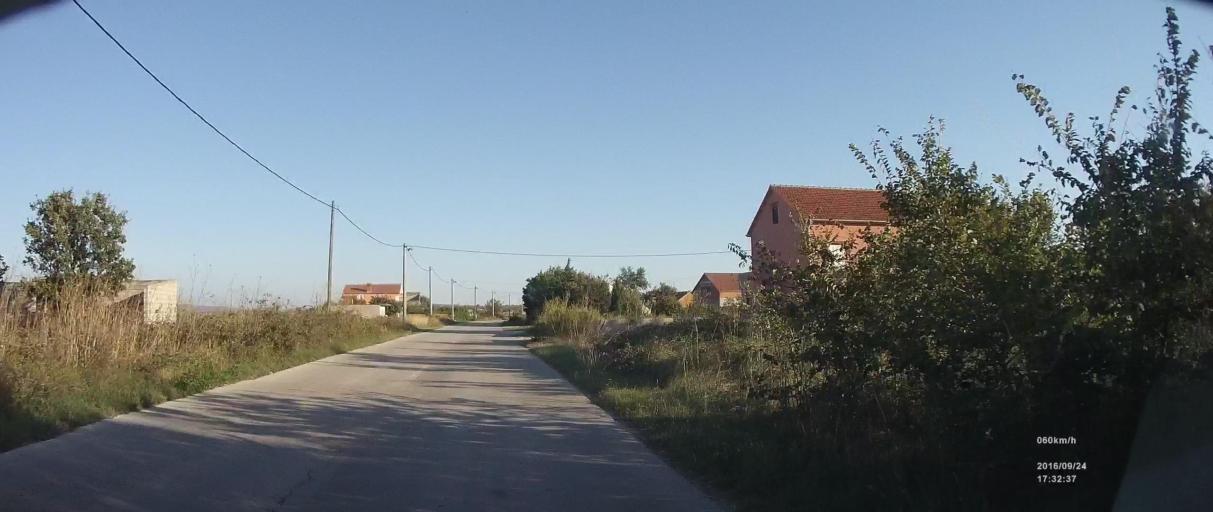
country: HR
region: Zadarska
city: Posedarje
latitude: 44.1810
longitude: 15.4516
